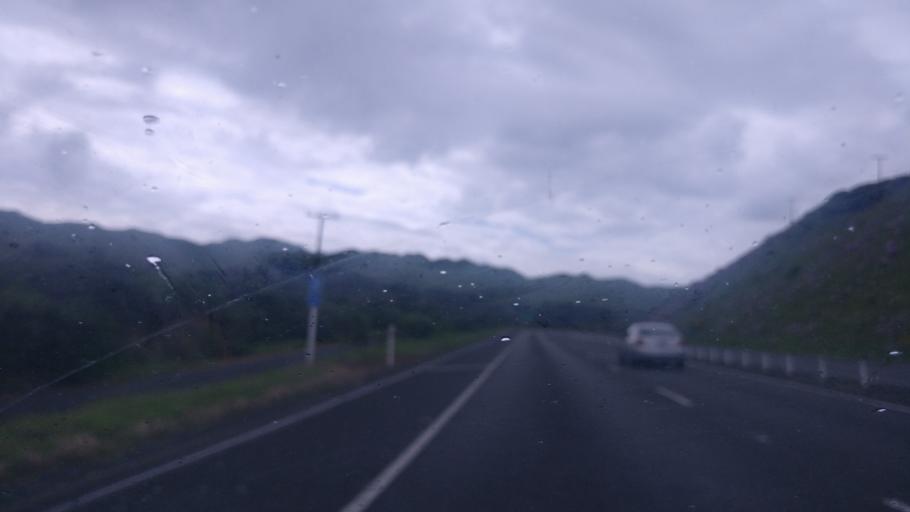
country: NZ
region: Wellington
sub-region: Porirua City
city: Porirua
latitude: -41.0633
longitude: 174.8770
